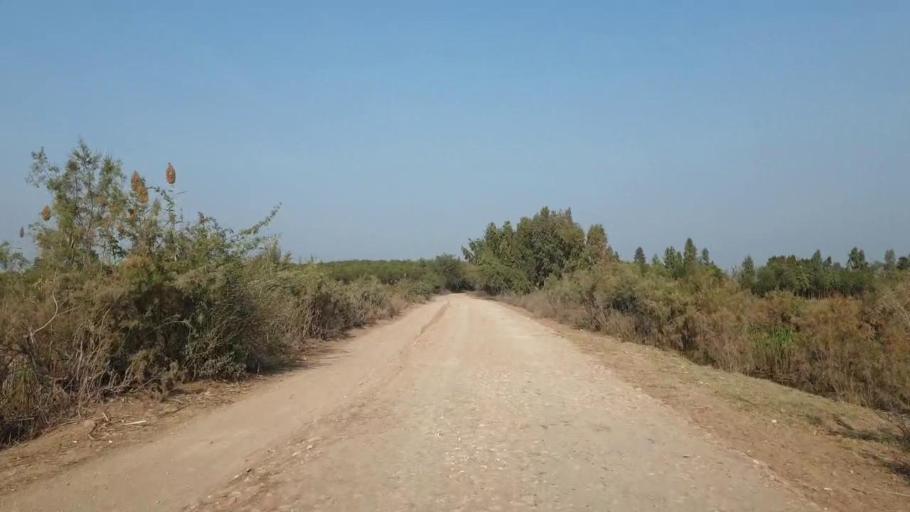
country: PK
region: Sindh
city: Tando Adam
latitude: 25.6581
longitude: 68.5831
